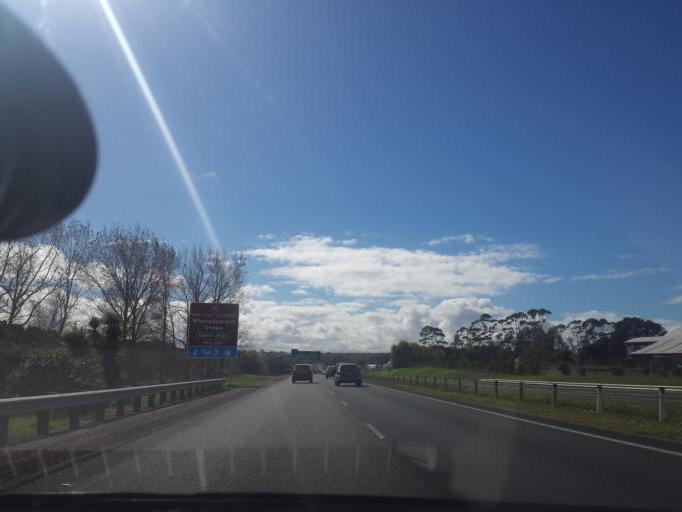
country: NZ
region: Auckland
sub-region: Auckland
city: Rothesay Bay
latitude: -36.6337
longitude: 174.6627
